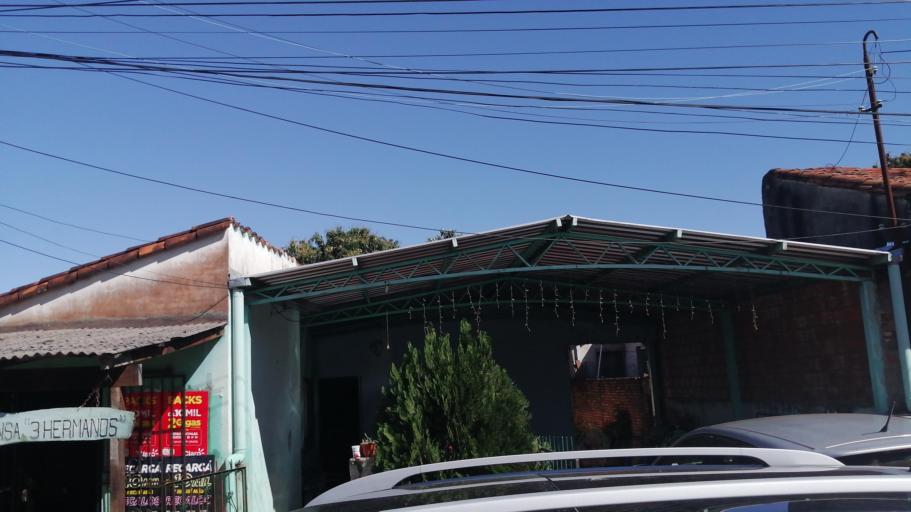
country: PY
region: Misiones
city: San Juan Bautista
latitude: -26.6785
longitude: -57.1442
